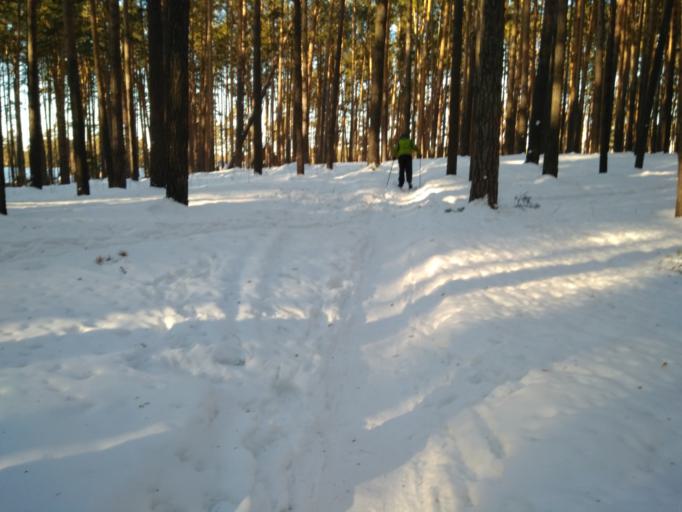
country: RU
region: Tomsk
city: Timiryazevskoye
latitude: 56.4861
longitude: 84.8799
